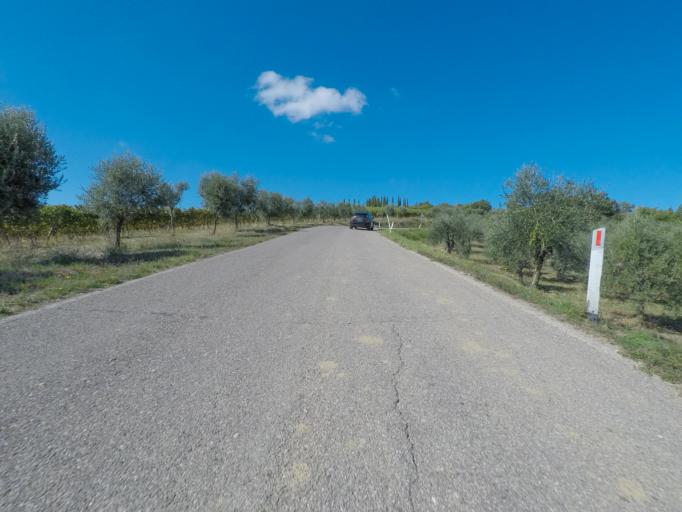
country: IT
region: Tuscany
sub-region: Provincia di Siena
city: Radda in Chianti
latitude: 43.5147
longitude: 11.4066
